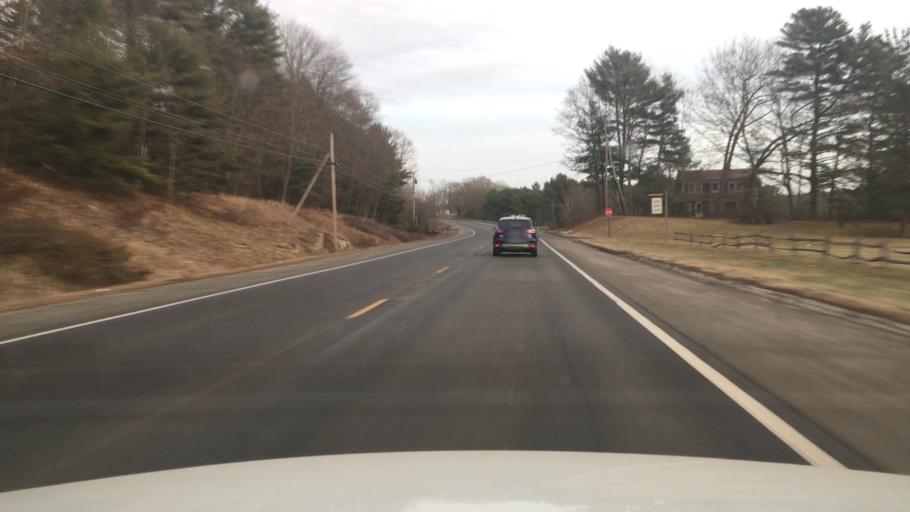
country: US
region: Maine
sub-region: Lincoln County
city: Edgecomb
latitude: 44.0118
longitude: -69.5937
